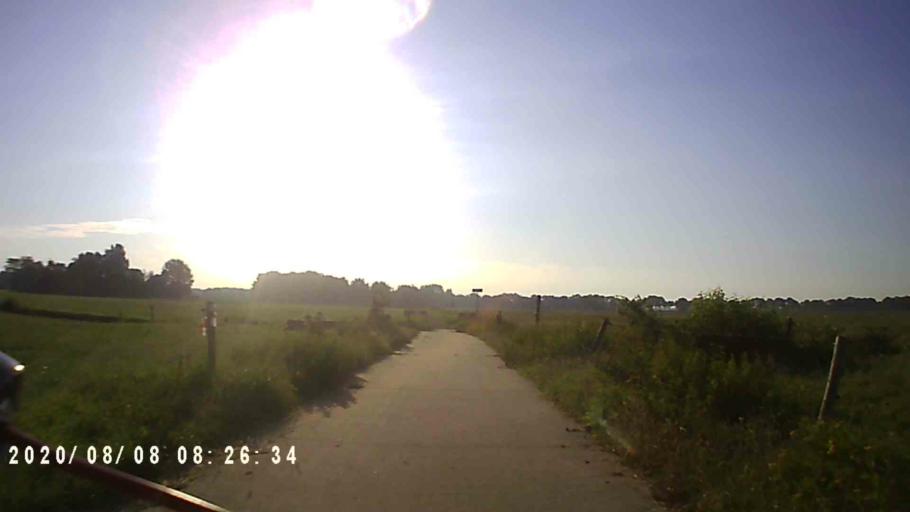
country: NL
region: Groningen
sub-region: Gemeente Leek
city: Leek
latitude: 53.0820
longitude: 6.3265
